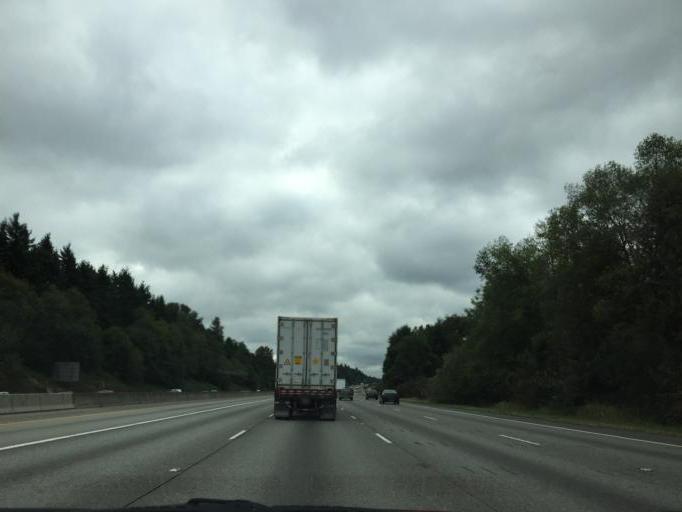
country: US
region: Washington
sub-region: King County
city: Des Moines
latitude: 47.3856
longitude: -122.2904
